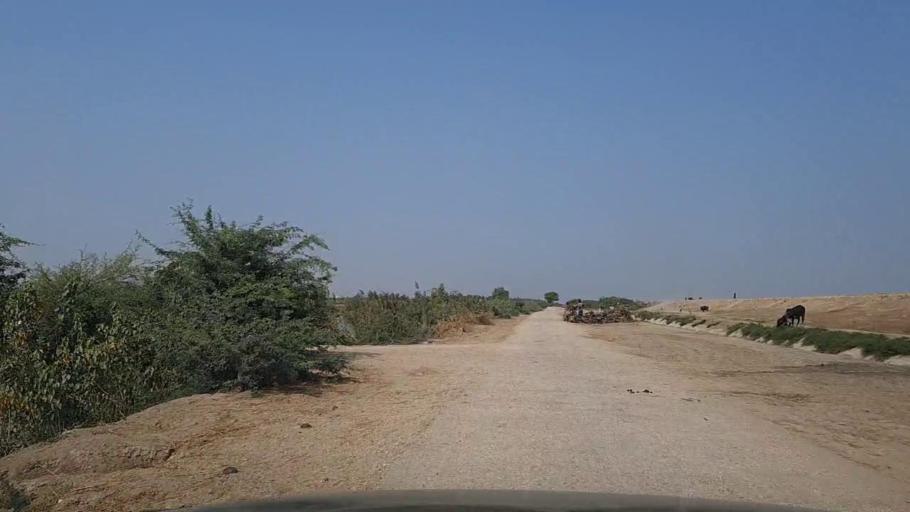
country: PK
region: Sindh
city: Chuhar Jamali
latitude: 24.5240
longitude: 67.9265
